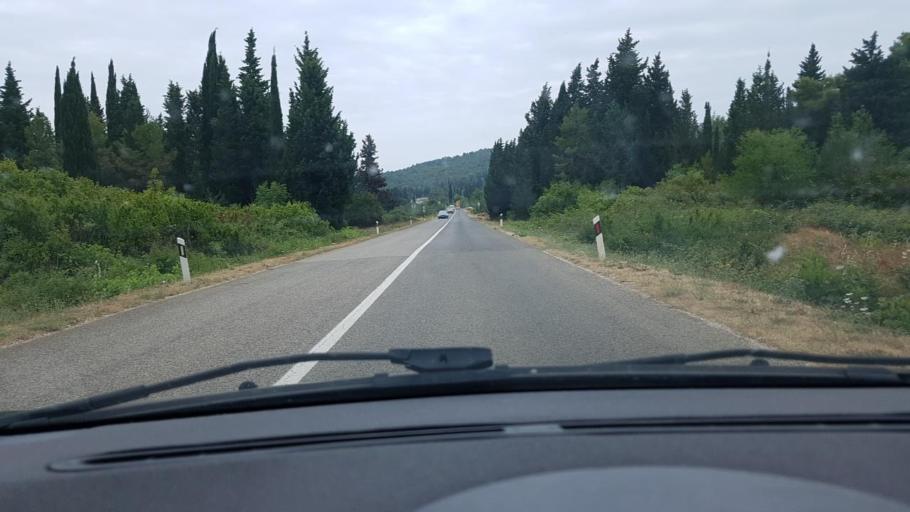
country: HR
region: Dubrovacko-Neretvanska
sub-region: Grad Korcula
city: Zrnovo
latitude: 42.9425
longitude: 17.1047
